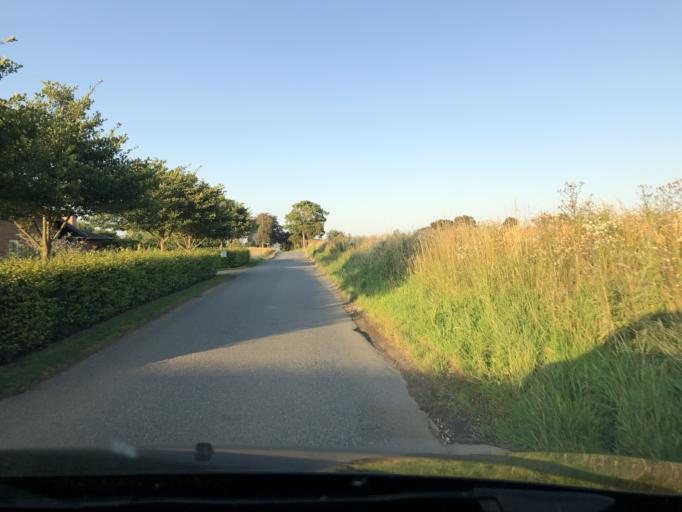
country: DK
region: South Denmark
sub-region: Vejle Kommune
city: Brejning
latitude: 55.6562
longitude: 9.7305
